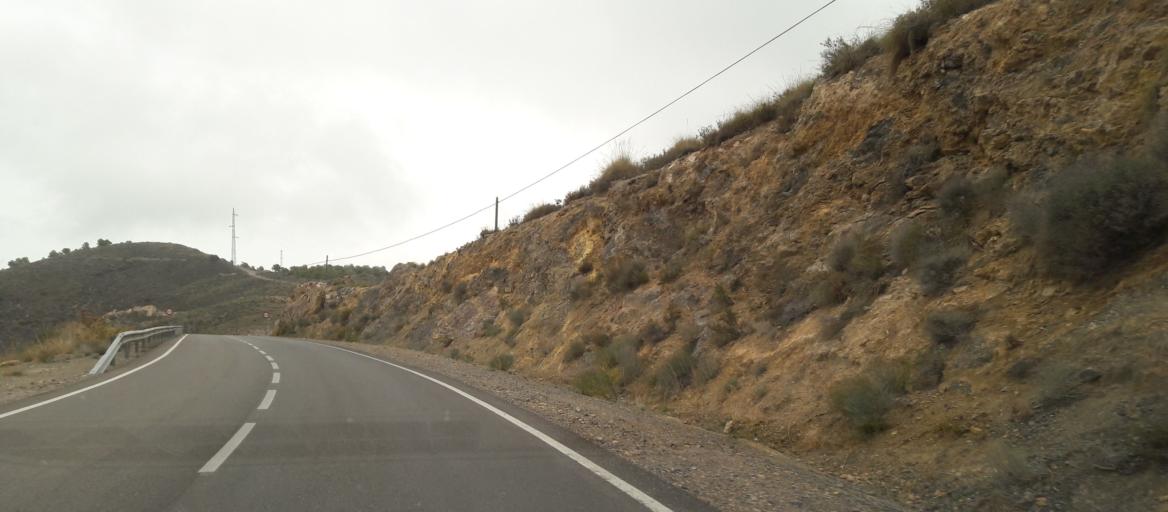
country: ES
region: Andalusia
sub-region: Provincia de Almeria
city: Enix
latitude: 36.8731
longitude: -2.6213
